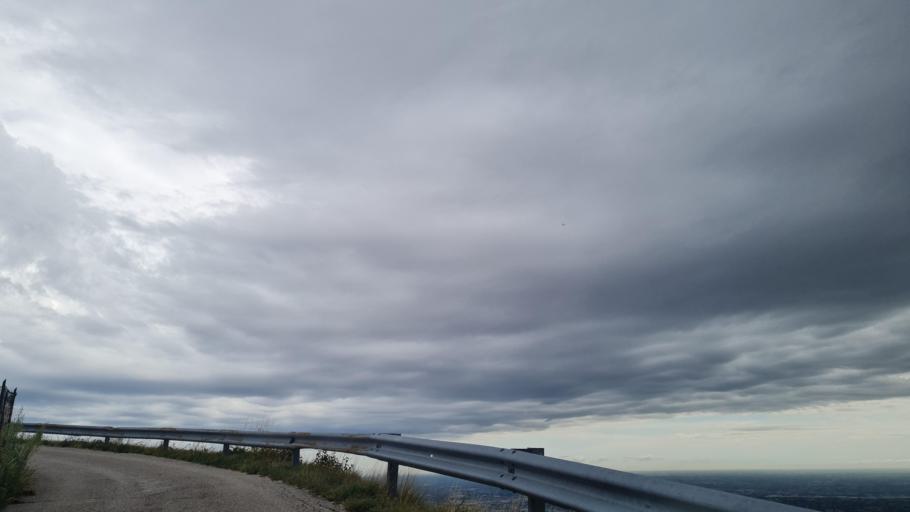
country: IT
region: Veneto
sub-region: Provincia di Vicenza
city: Marostica
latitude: 45.7830
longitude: 11.6625
